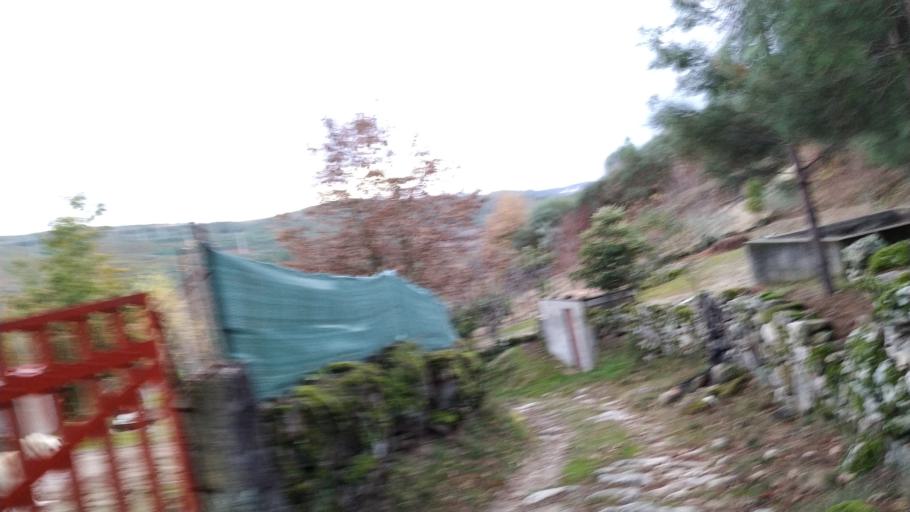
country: PT
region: Vila Real
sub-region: Vila Real
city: Vila Real
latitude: 41.3514
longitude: -7.7136
